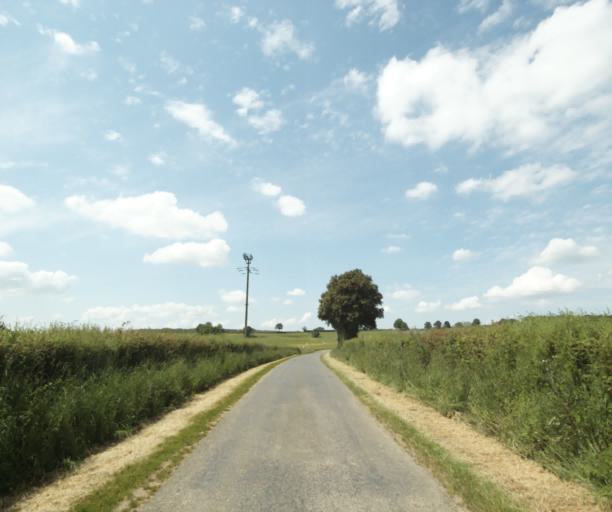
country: FR
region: Bourgogne
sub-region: Departement de Saone-et-Loire
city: Perrecy-les-Forges
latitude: 46.5840
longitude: 4.1428
